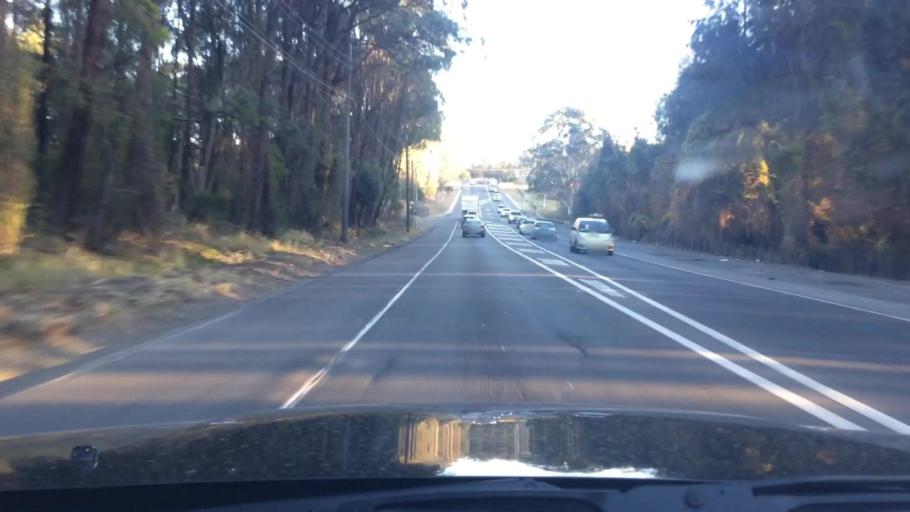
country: AU
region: New South Wales
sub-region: Fairfield
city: Carramar
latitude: -33.8969
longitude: 150.9728
